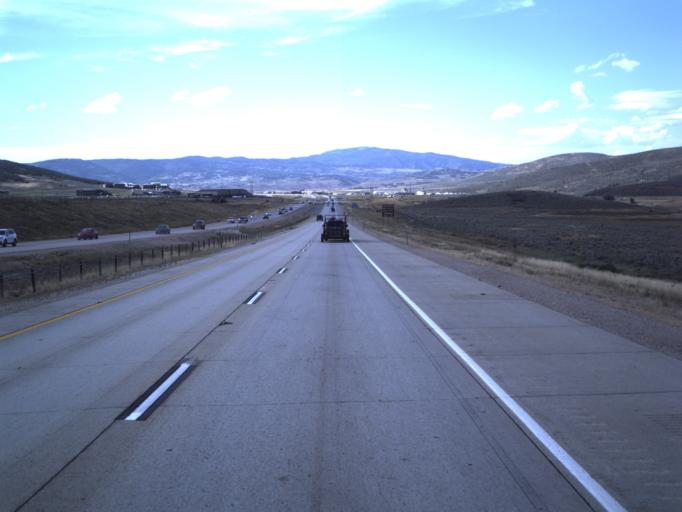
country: US
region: Utah
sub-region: Summit County
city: Park City
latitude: 40.6655
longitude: -111.4589
